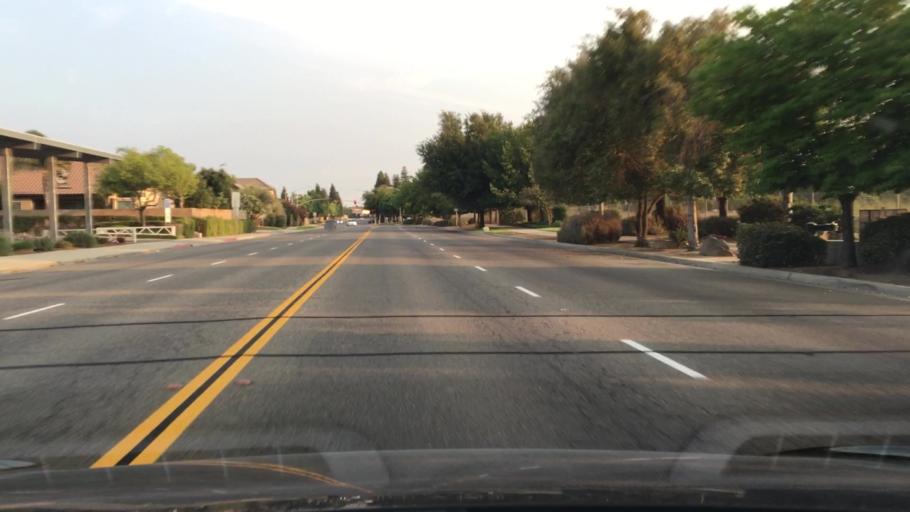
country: US
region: California
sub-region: Fresno County
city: Clovis
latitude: 36.8471
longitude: -119.6931
